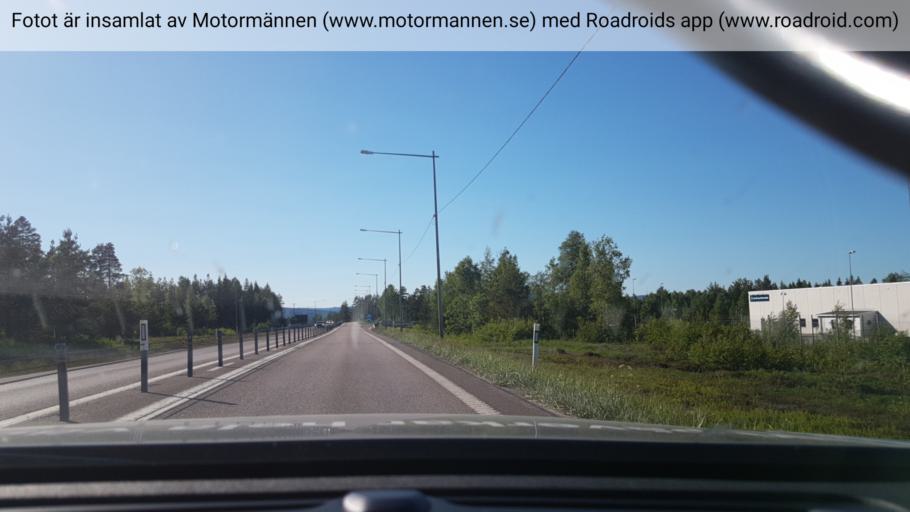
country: SE
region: Vaesternorrland
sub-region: Haernoesands Kommun
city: Haernoesand
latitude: 62.6524
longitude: 17.8866
